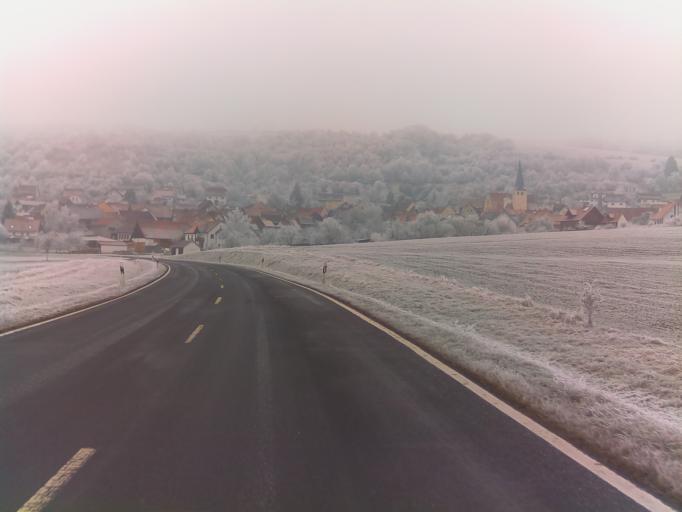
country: DE
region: Bavaria
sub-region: Regierungsbezirk Unterfranken
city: Oberelsbach
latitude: 50.4215
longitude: 10.0839
